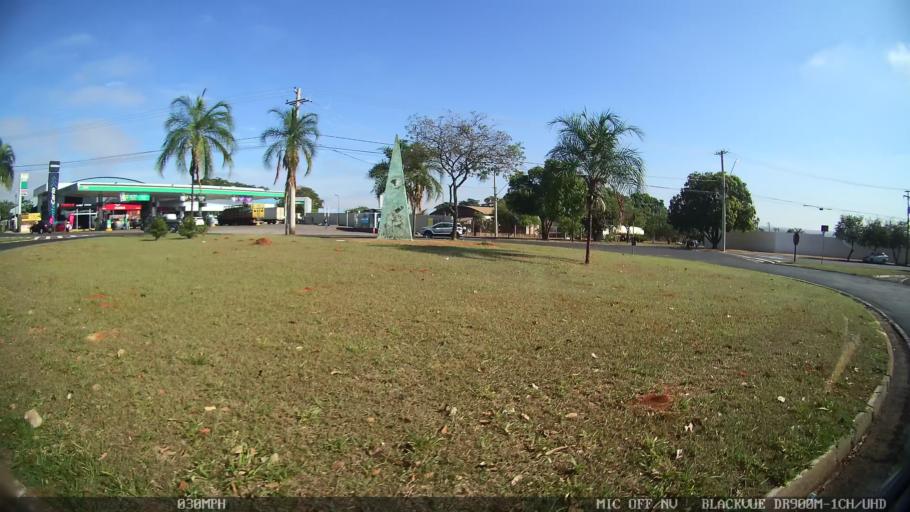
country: BR
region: Sao Paulo
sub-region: Sao Jose Do Rio Preto
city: Sao Jose do Rio Preto
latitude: -20.8153
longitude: -49.4100
